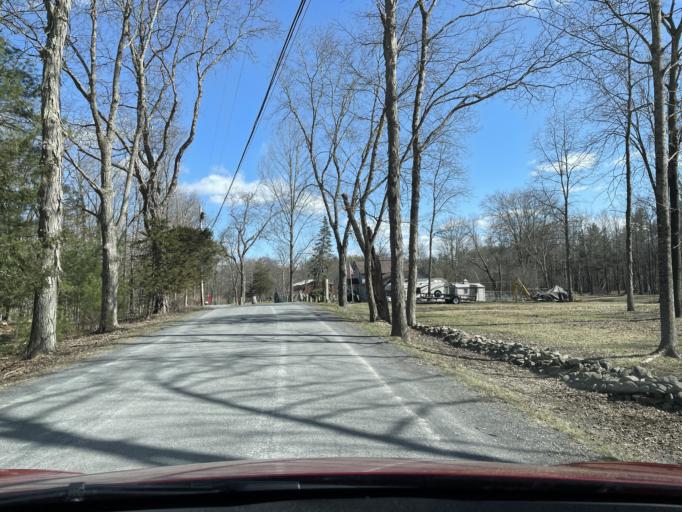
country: US
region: New York
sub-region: Ulster County
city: Zena
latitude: 42.0288
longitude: -74.0932
